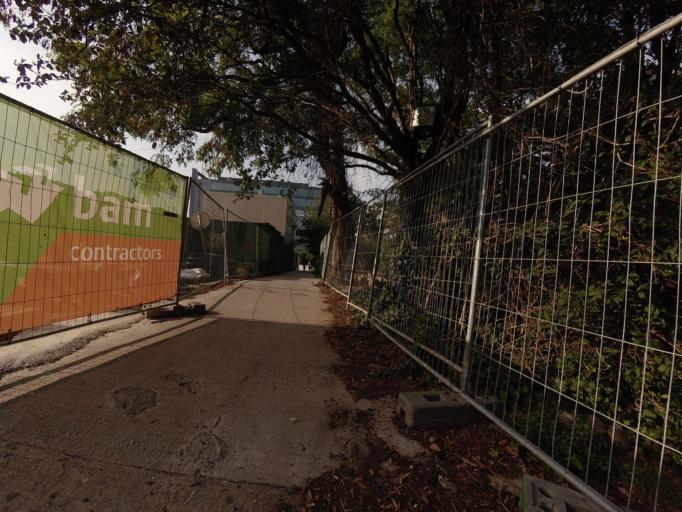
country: BE
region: Brussels Capital
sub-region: Bruxelles-Capitale
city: Brussels
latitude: 50.8501
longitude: 4.4029
